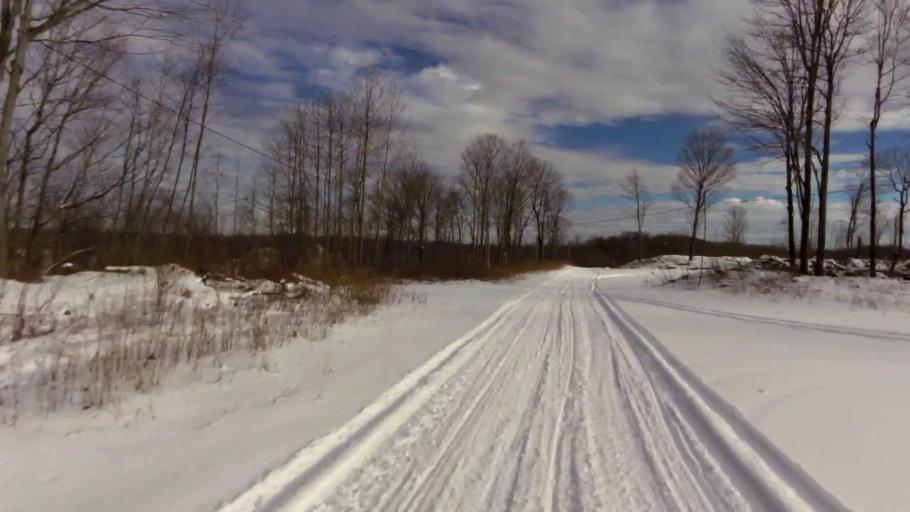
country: US
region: Pennsylvania
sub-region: McKean County
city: Foster Brook
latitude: 42.0056
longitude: -78.5850
